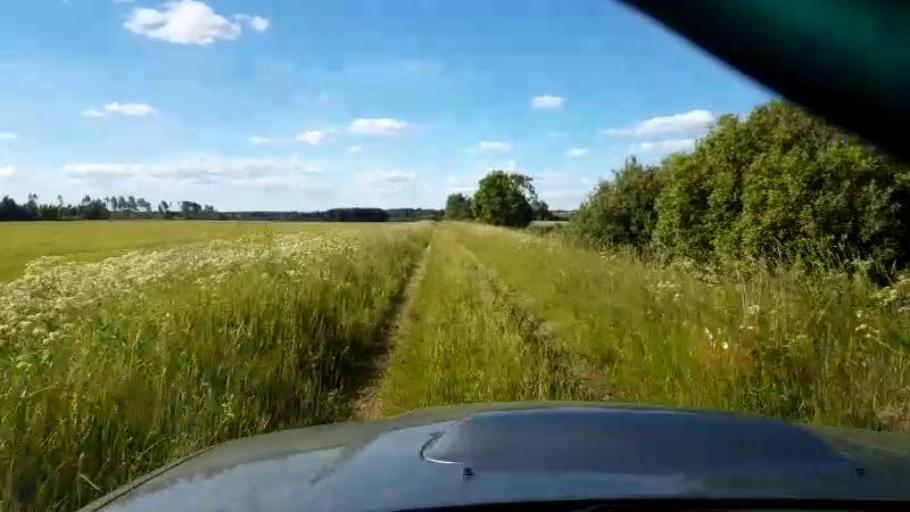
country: EE
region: Paernumaa
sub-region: Sauga vald
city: Sauga
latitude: 58.5003
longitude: 24.5910
